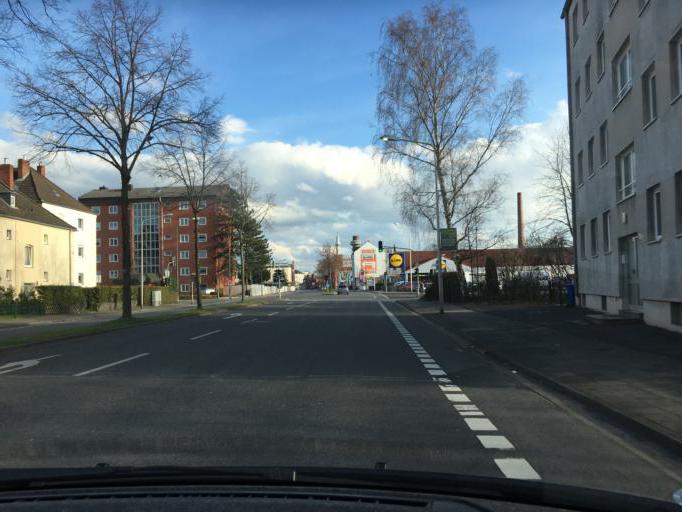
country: DE
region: North Rhine-Westphalia
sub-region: Regierungsbezirk Koln
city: Dueren
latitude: 50.8118
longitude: 6.4719
